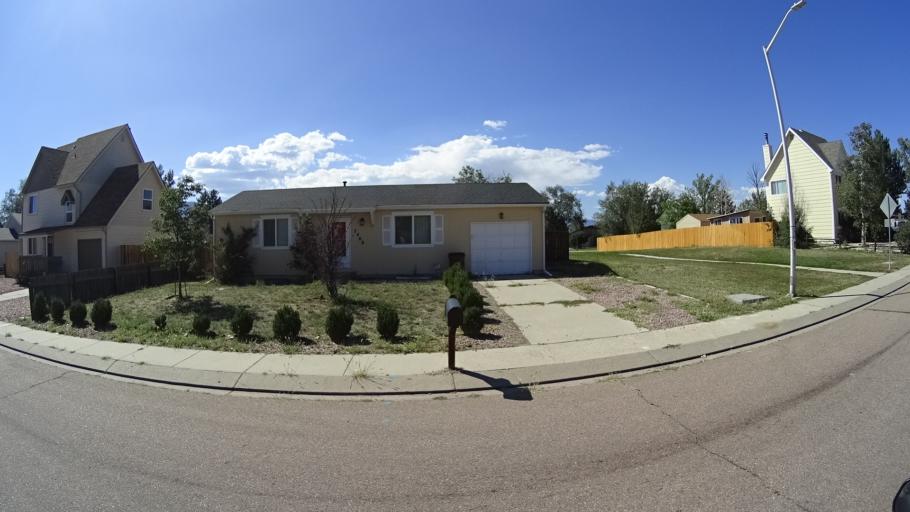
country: US
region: Colorado
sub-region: El Paso County
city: Stratmoor
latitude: 38.7840
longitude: -104.7465
